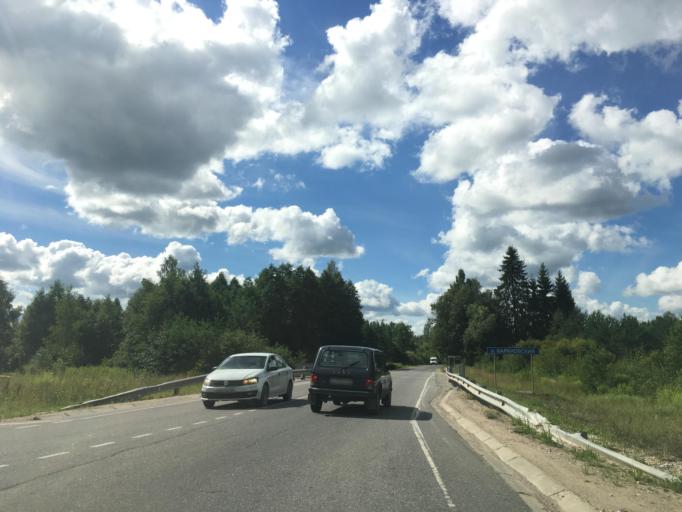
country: RU
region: Pskov
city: Pskov
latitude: 57.6957
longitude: 28.1800
